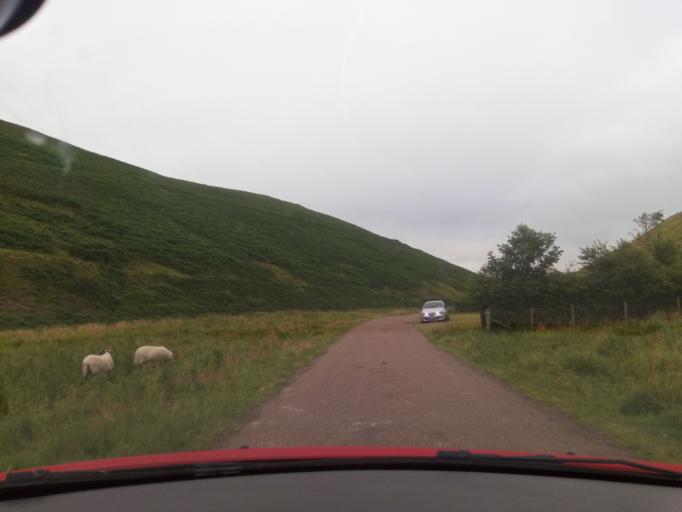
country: GB
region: England
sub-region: Northumberland
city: Rochester
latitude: 55.3694
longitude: -2.2102
